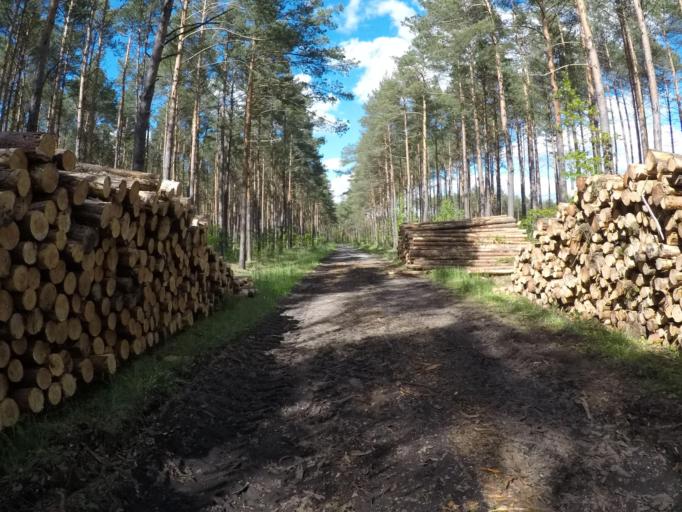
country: PL
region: Swietokrzyskie
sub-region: Powiat kielecki
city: Kostomloty Drugie
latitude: 50.8867
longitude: 20.5359
